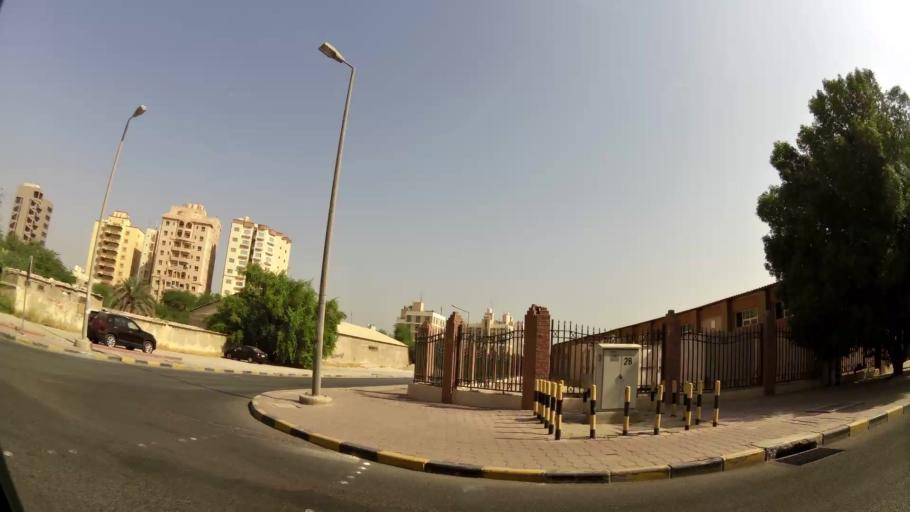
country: KW
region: Muhafazat Hawalli
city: Hawalli
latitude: 29.3447
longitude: 48.0200
